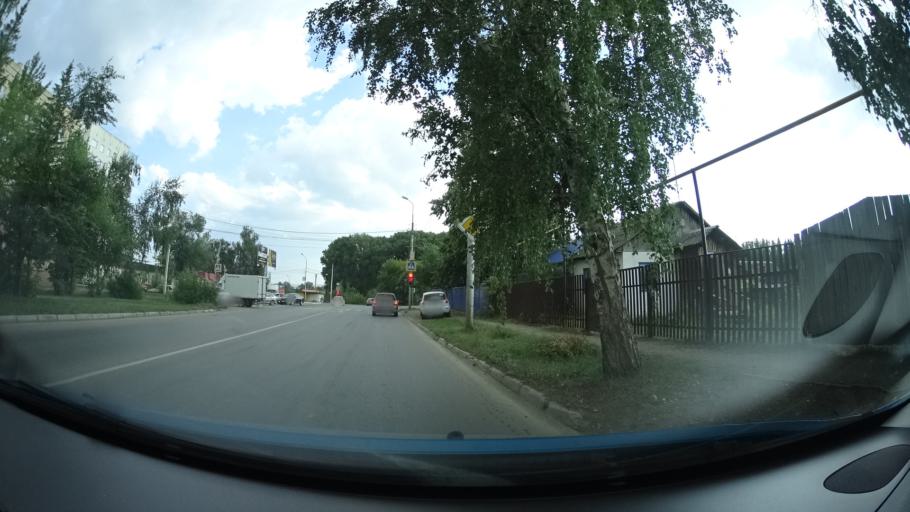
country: RU
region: Bashkortostan
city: Oktyabr'skiy
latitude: 54.4854
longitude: 53.4443
